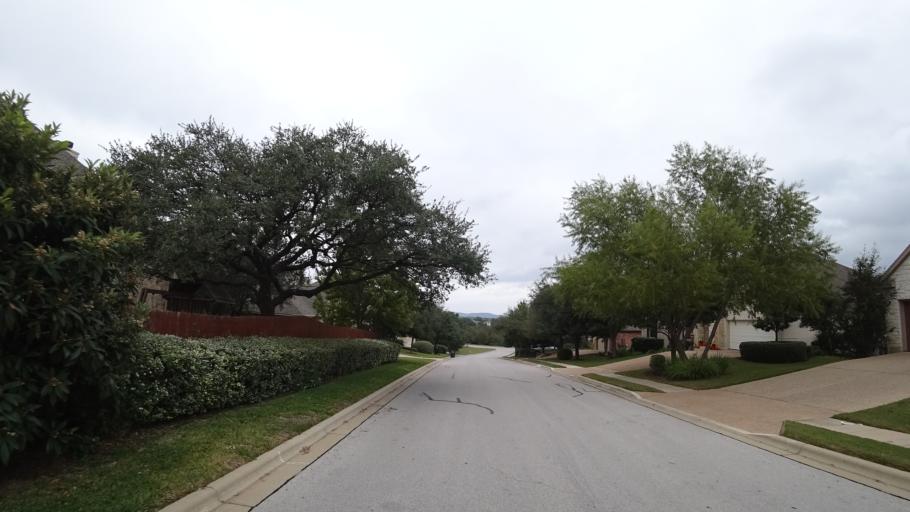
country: US
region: Texas
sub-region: Travis County
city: Hudson Bend
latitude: 30.3603
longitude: -97.9075
